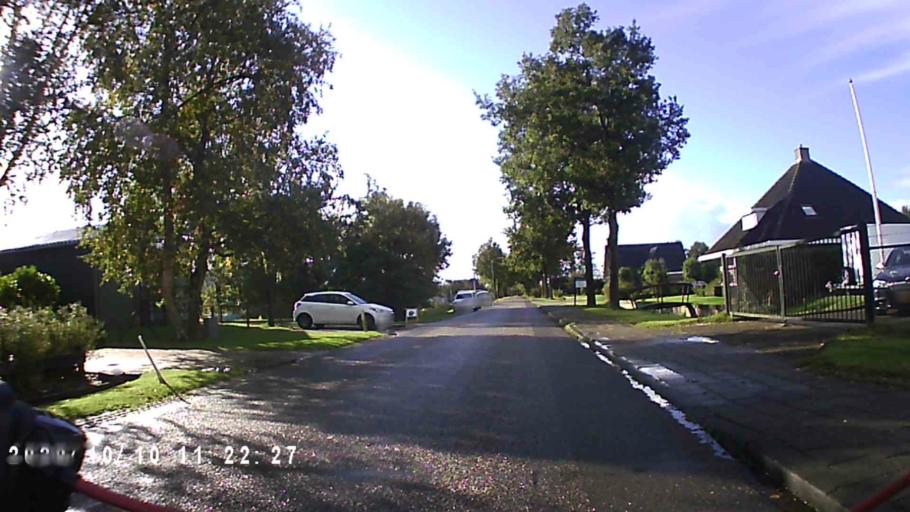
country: NL
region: Friesland
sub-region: Gemeente Smallingerland
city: Drachtstercompagnie
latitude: 53.0931
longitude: 6.1782
